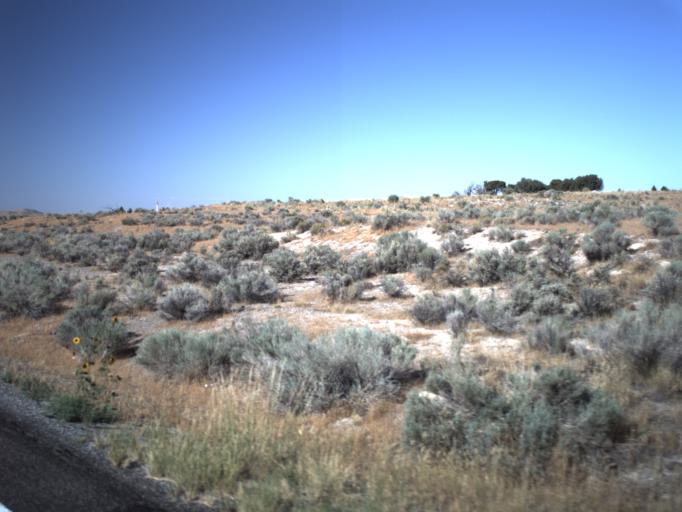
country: US
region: Utah
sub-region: Juab County
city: Mona
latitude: 39.7482
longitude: -112.1849
